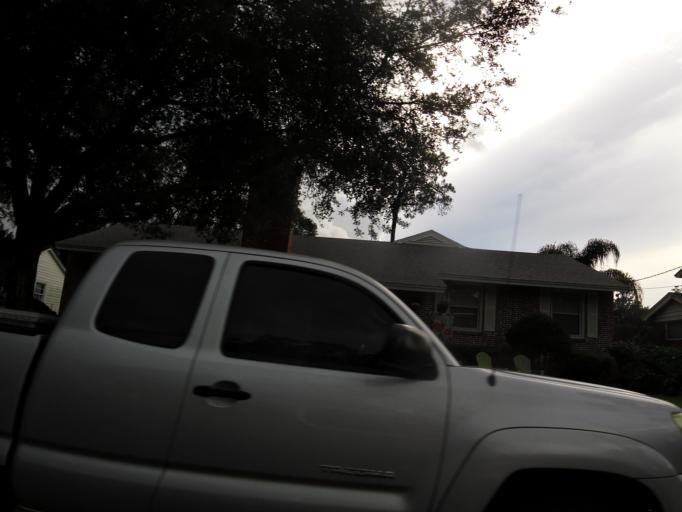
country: US
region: Florida
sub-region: Duval County
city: Jacksonville
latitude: 30.3079
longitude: -81.6355
